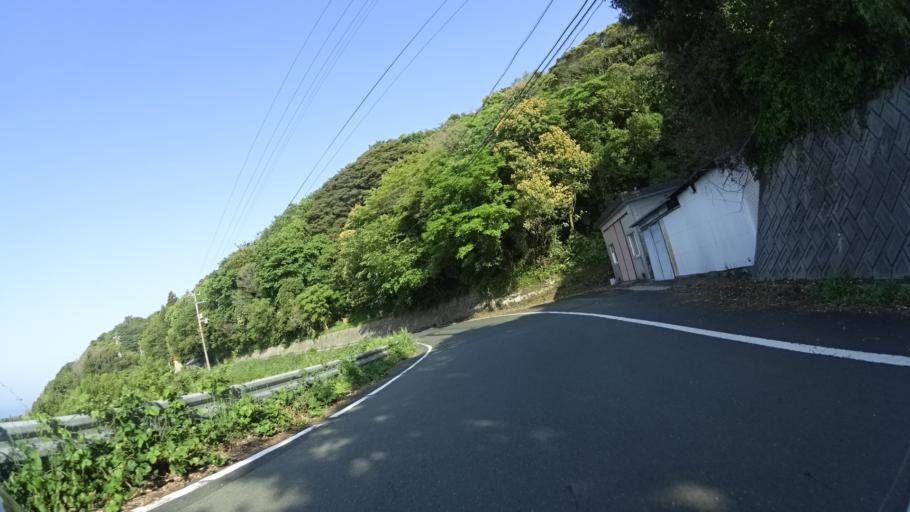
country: JP
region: Ehime
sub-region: Nishiuwa-gun
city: Ikata-cho
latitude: 33.3842
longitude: 132.0868
